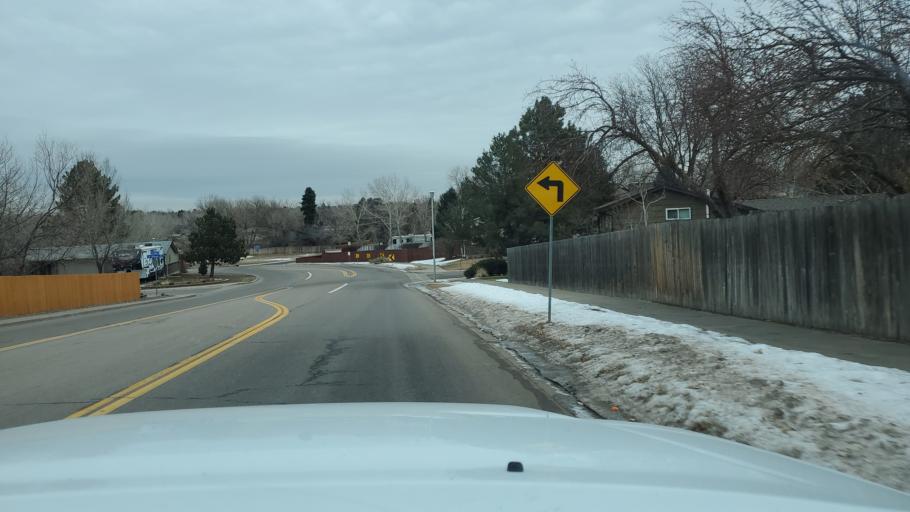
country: US
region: Colorado
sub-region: Arapahoe County
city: Greenwood Village
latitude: 39.6029
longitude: -104.9379
